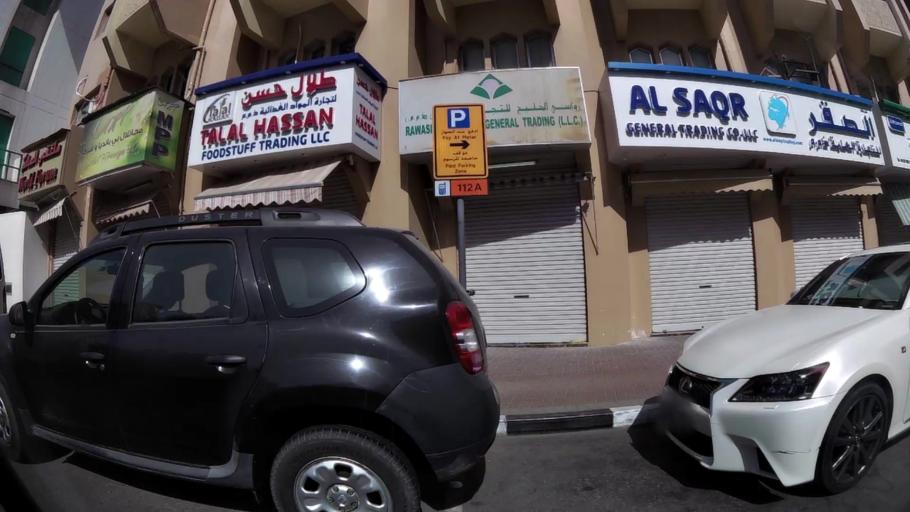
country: AE
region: Ash Shariqah
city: Sharjah
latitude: 25.2673
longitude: 55.2938
